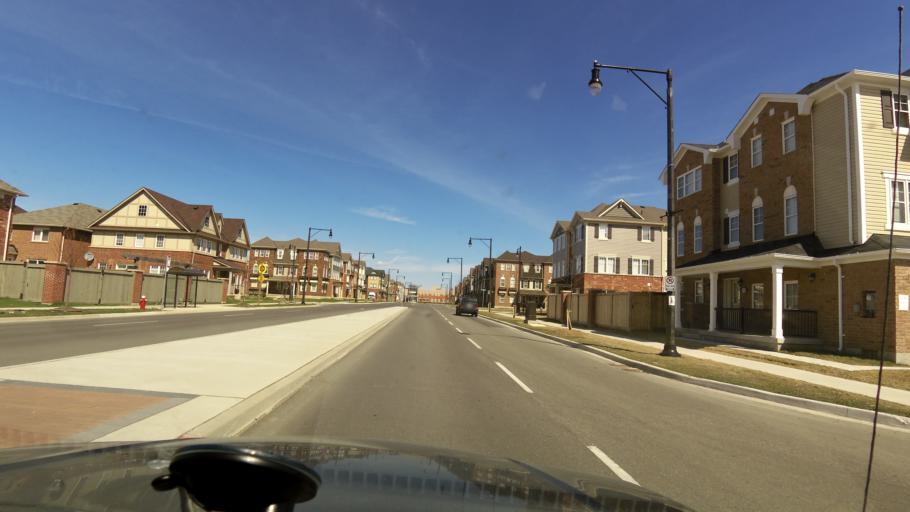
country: CA
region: Ontario
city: Brampton
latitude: 43.6762
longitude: -79.8279
